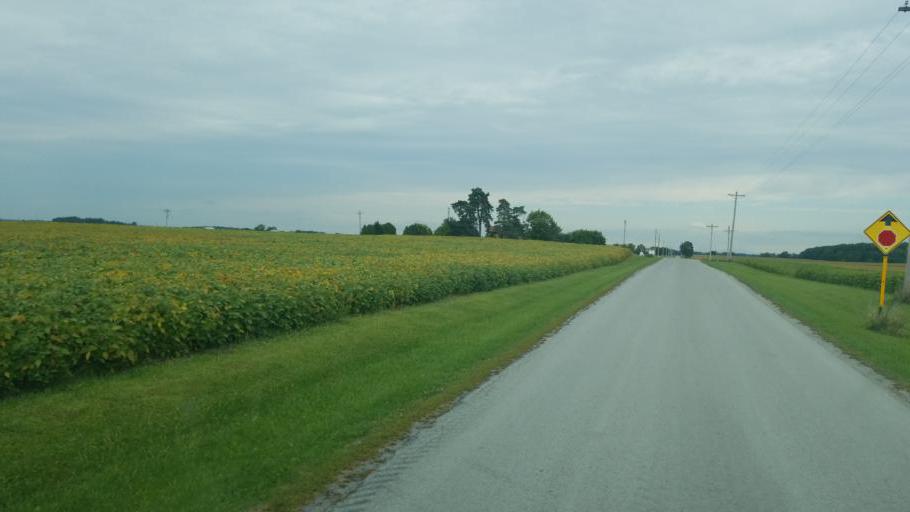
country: US
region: Ohio
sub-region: Wyandot County
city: Upper Sandusky
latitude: 40.7875
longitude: -83.1885
